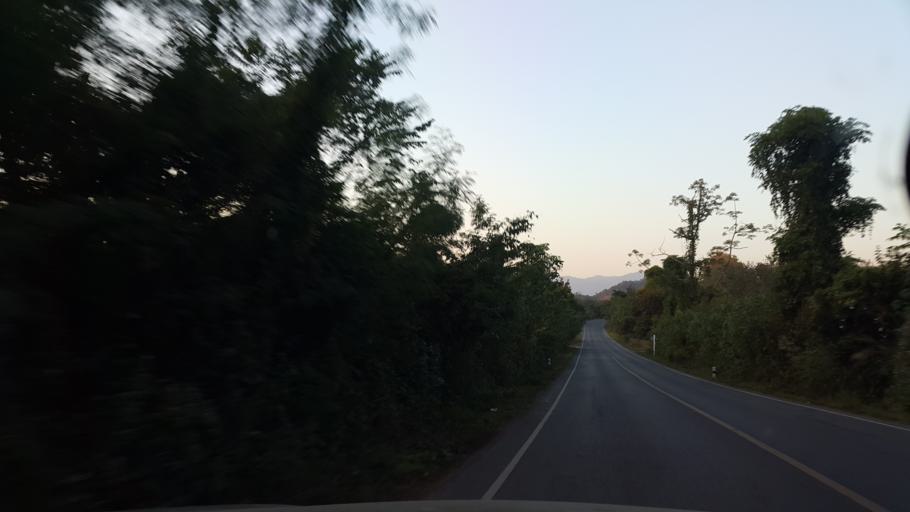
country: TH
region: Phrae
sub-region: Amphoe Wang Chin
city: Wang Chin
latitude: 17.8350
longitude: 99.6421
